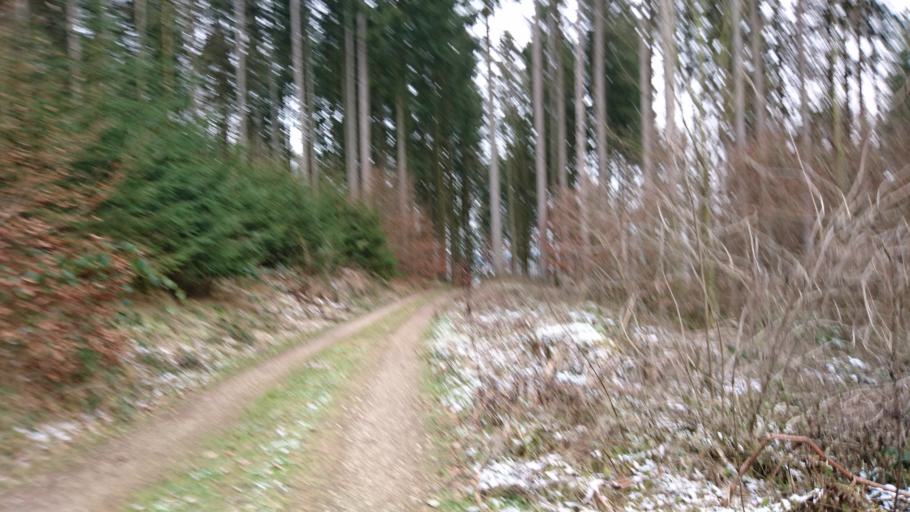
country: DE
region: Bavaria
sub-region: Swabia
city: Zusmarshausen
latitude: 48.4332
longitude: 10.6073
